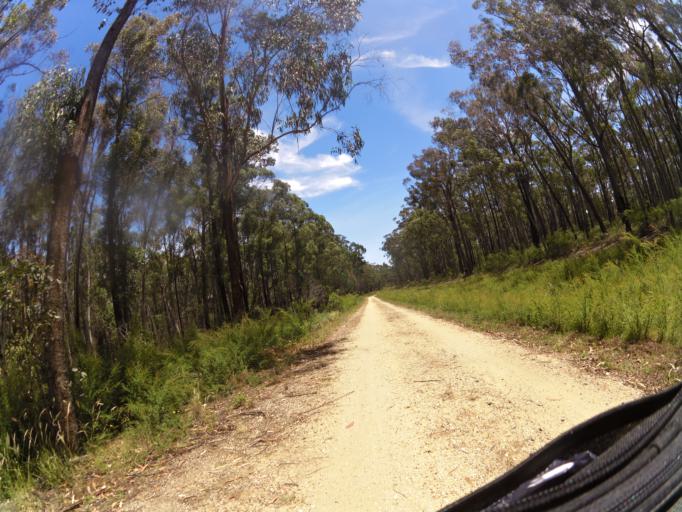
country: AU
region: Victoria
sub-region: East Gippsland
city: Lakes Entrance
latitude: -37.7590
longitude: 147.9409
